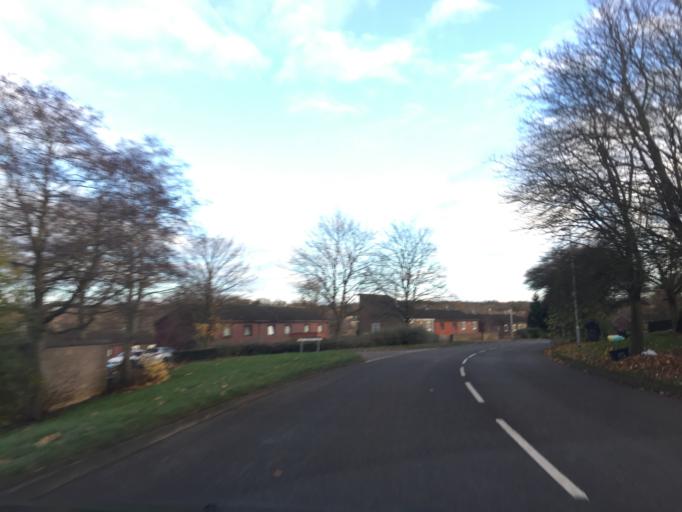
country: GB
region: England
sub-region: Northamptonshire
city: Northampton
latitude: 52.2731
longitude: -0.8368
